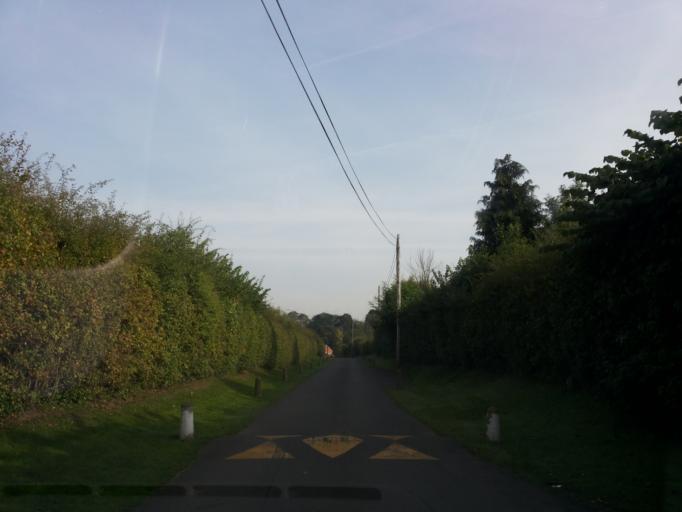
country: GB
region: England
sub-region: Worcestershire
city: Stourport-on-Severn
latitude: 52.3465
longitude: -2.2979
